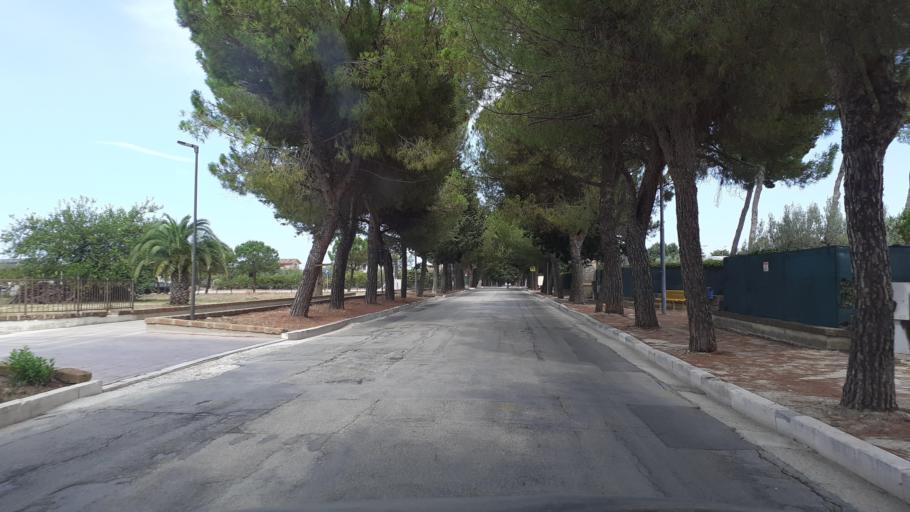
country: IT
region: Abruzzo
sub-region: Provincia di Chieti
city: Fossacesia
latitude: 42.2485
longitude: 14.4863
